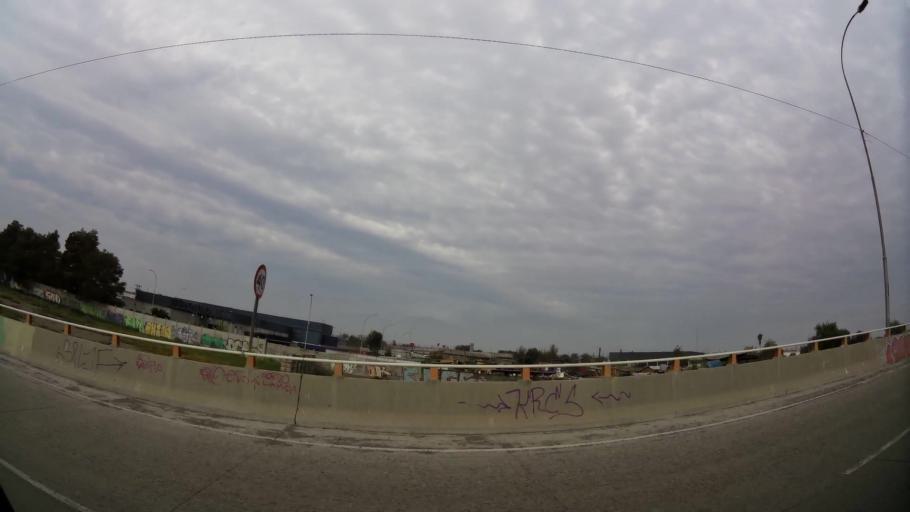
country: CL
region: Santiago Metropolitan
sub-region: Provincia de Santiago
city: Lo Prado
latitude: -33.5241
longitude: -70.7553
